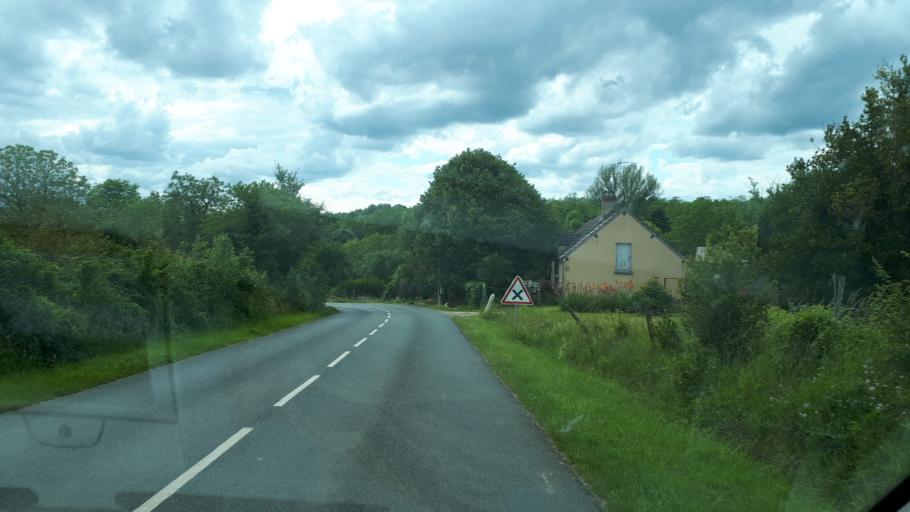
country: FR
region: Centre
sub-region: Departement du Cher
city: Gracay
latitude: 47.1368
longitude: 1.8774
